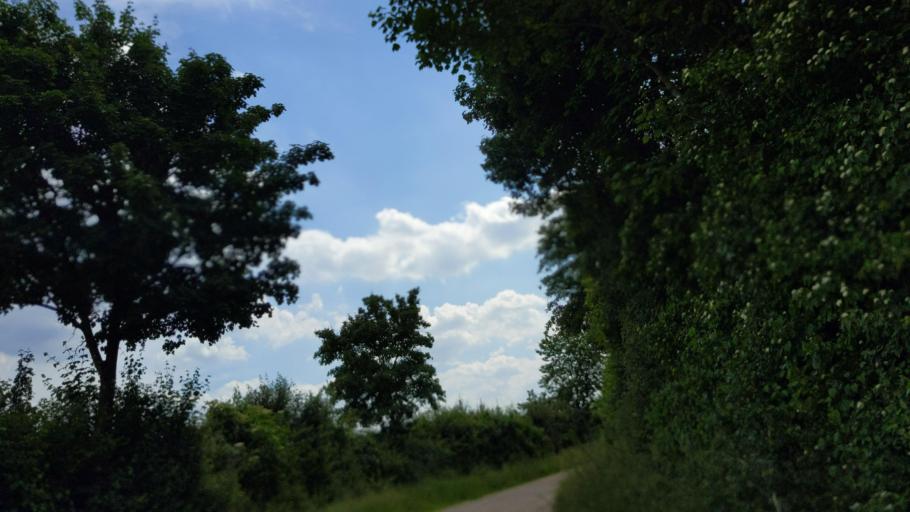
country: DE
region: Schleswig-Holstein
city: Buchholz
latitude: 53.7521
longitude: 10.7607
